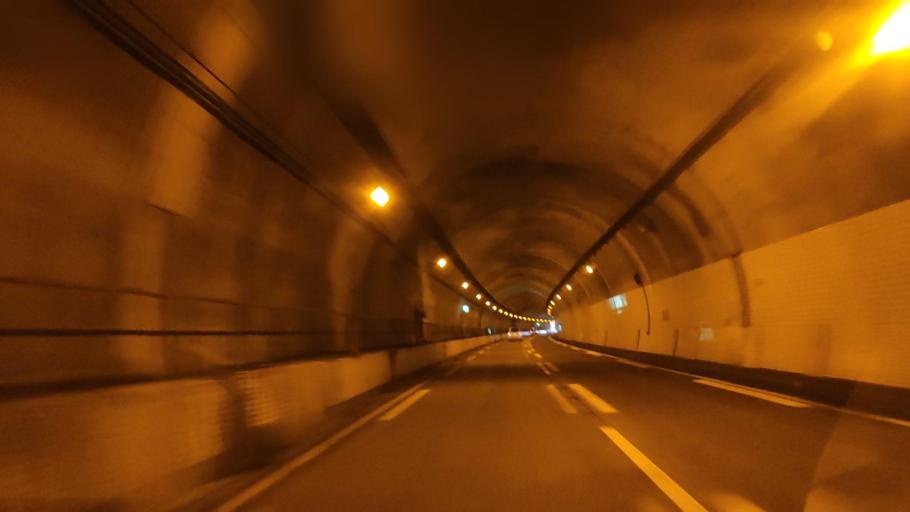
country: JP
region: Niigata
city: Joetsu
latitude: 37.1374
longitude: 138.0611
